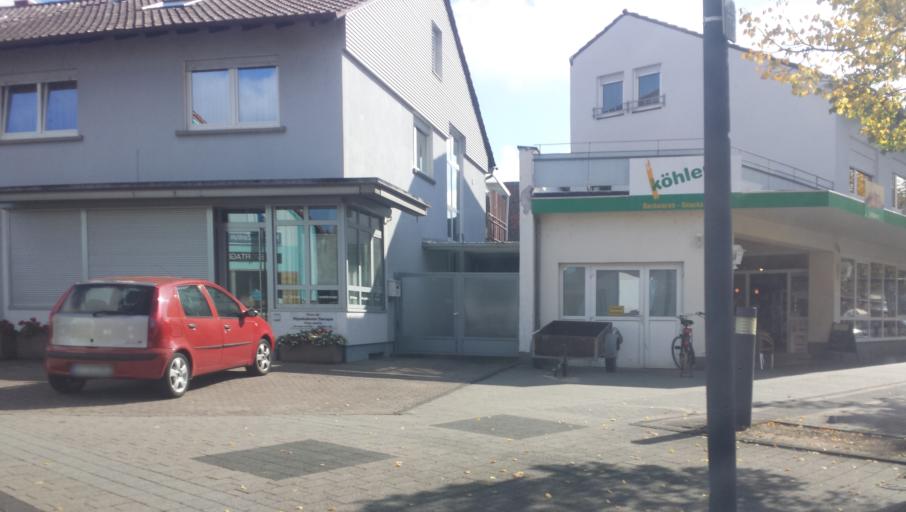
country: DE
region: Baden-Wuerttemberg
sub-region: Karlsruhe Region
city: Waghausel
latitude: 49.2265
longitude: 8.5180
